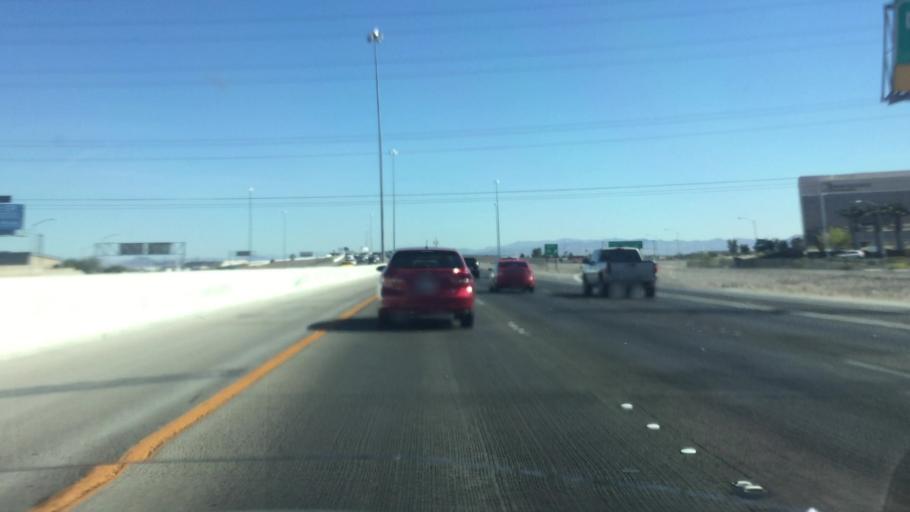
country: US
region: Nevada
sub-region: Clark County
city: Enterprise
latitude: 36.0674
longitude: -115.2133
